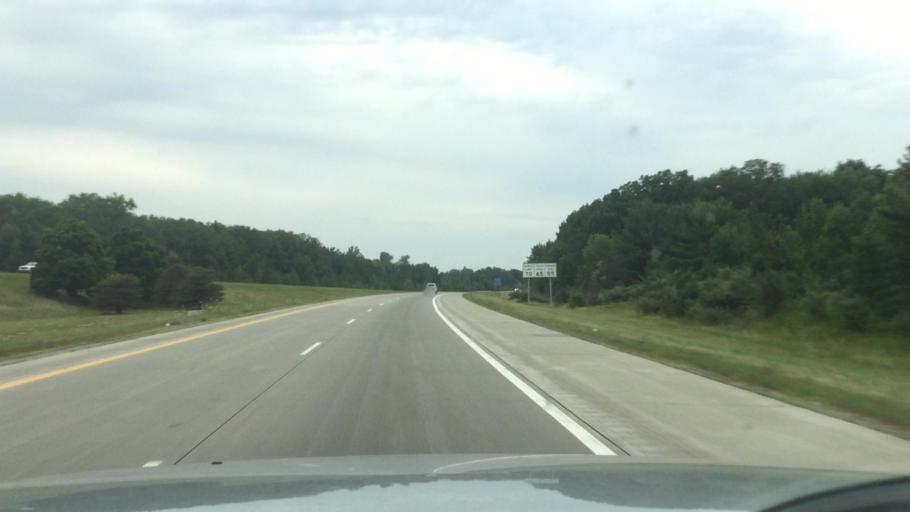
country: US
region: Michigan
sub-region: Genesee County
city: Grand Blanc
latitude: 42.9230
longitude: -83.6800
